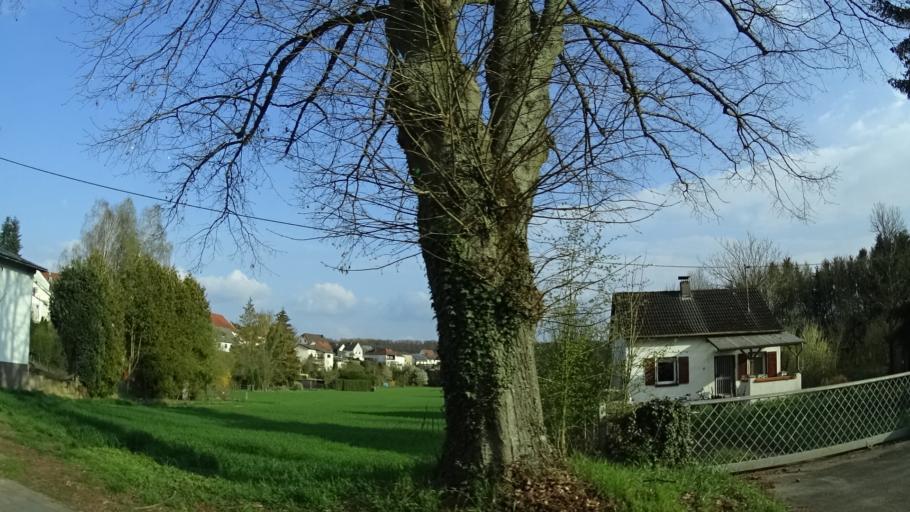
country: DE
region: Rheinland-Pfalz
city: Sponheim
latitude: 49.8451
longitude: 7.7224
